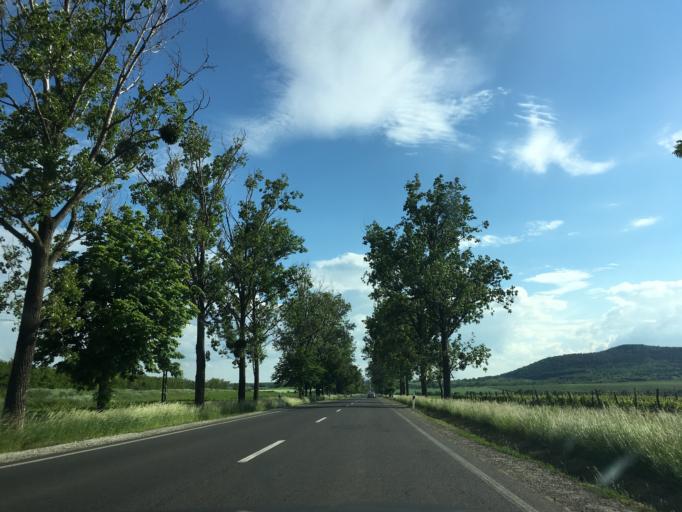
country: HU
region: Borsod-Abauj-Zemplen
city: Sarospatak
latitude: 48.3041
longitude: 21.5208
